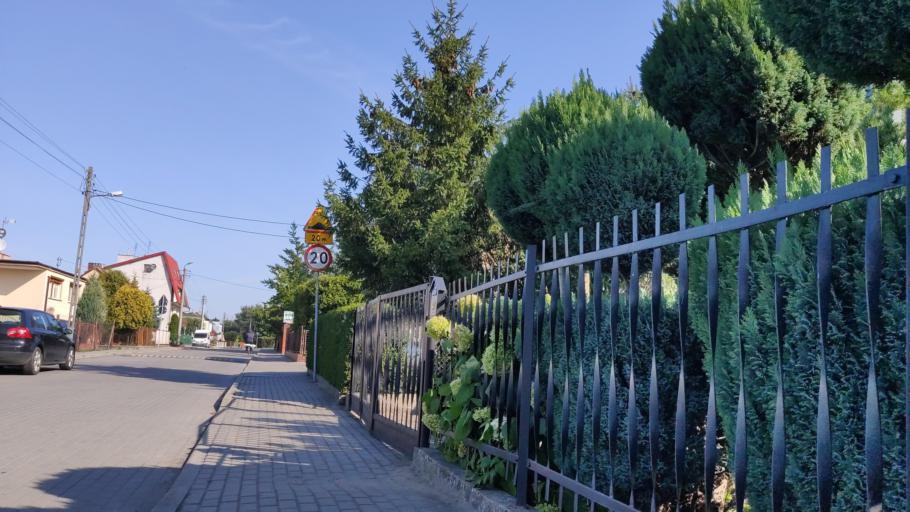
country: PL
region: Kujawsko-Pomorskie
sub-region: Powiat zninski
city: Znin
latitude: 52.8504
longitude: 17.7268
